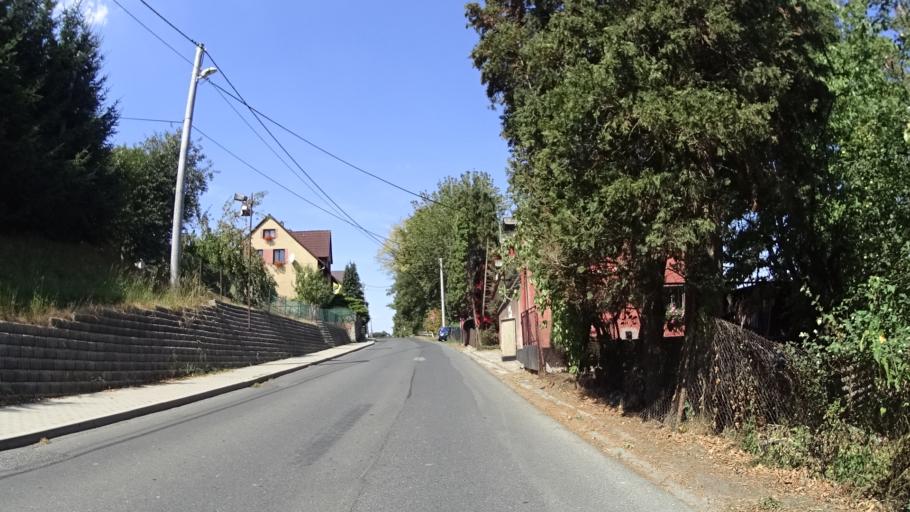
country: CZ
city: Hradek nad Nisou
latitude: 50.8346
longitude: 14.8670
